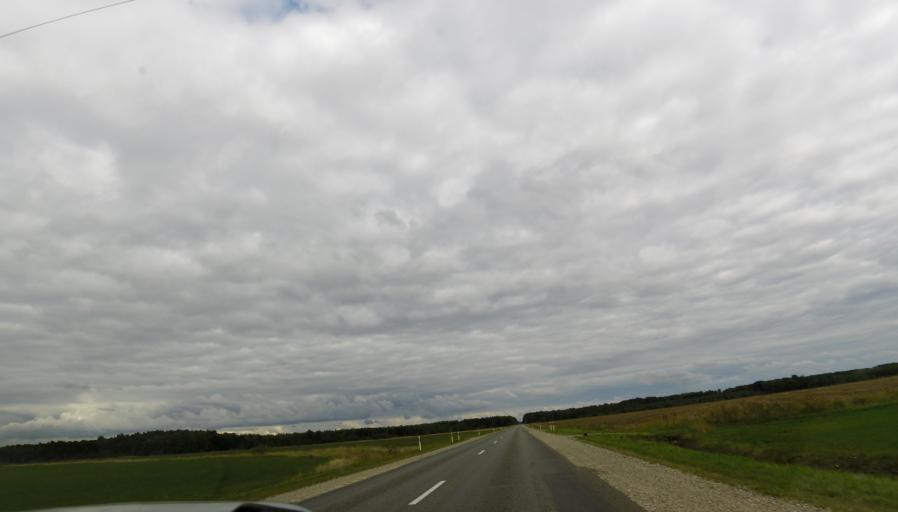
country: LT
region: Panevezys
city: Pasvalys
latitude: 56.0283
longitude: 24.2567
